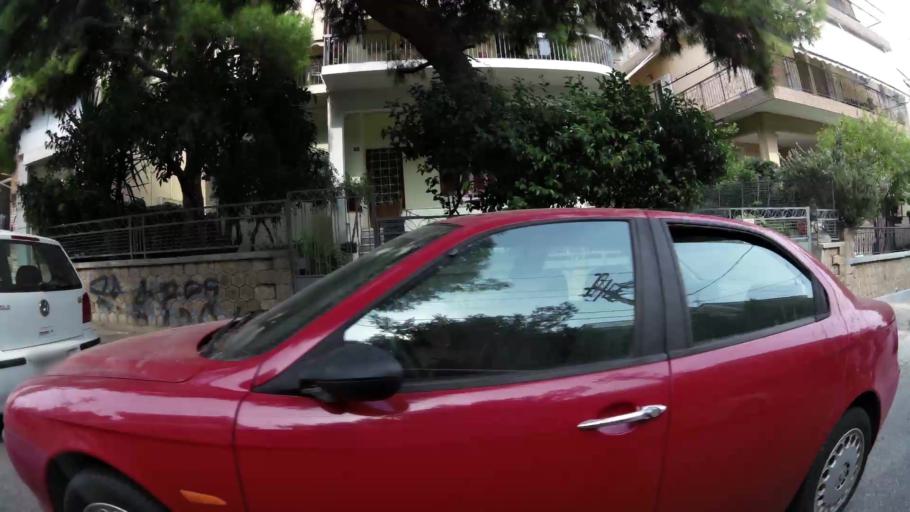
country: GR
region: Attica
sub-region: Nomarchia Athinas
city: Chaidari
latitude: 38.0154
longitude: 23.6497
